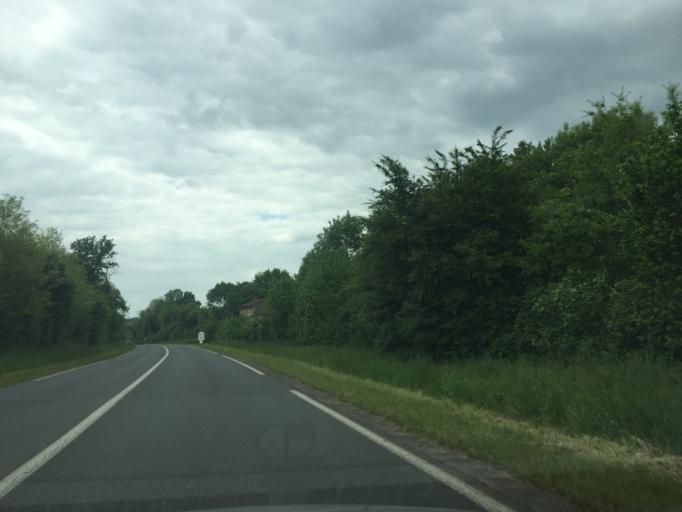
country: FR
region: Poitou-Charentes
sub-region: Departement de la Vienne
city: Lusignan
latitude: 46.4538
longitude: 0.1420
